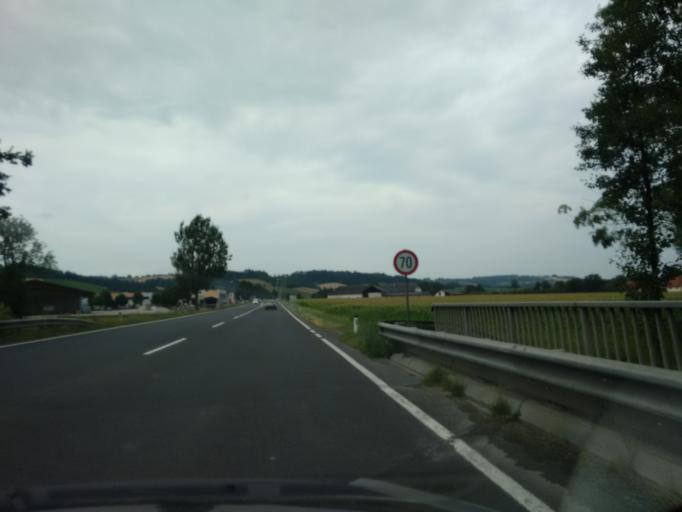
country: AT
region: Upper Austria
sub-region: Politischer Bezirk Grieskirchen
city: Bad Schallerbach
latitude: 48.2019
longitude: 13.9274
